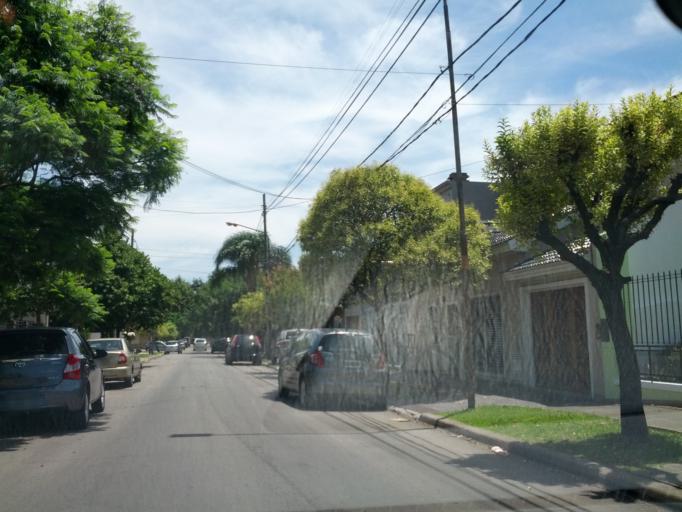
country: AR
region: Buenos Aires
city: San Justo
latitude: -34.6440
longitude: -58.5743
